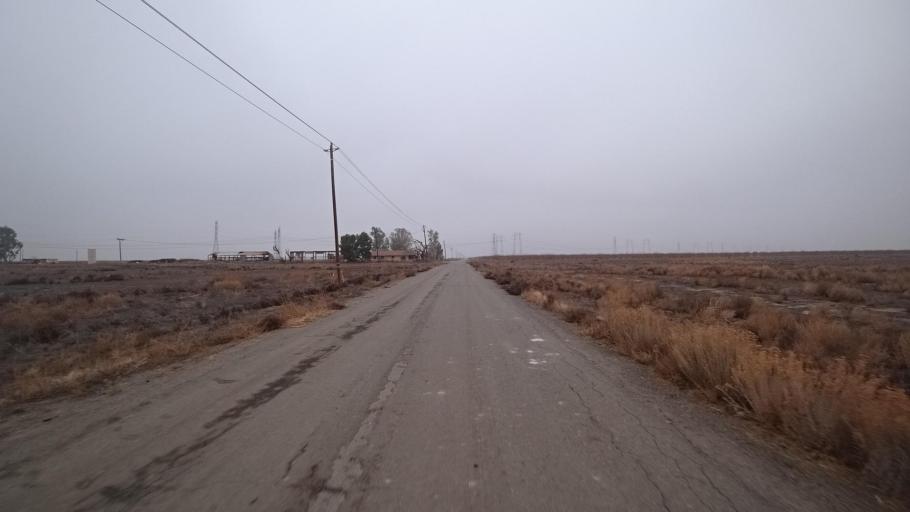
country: US
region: California
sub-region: Kern County
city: Lost Hills
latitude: 35.5864
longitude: -119.5971
